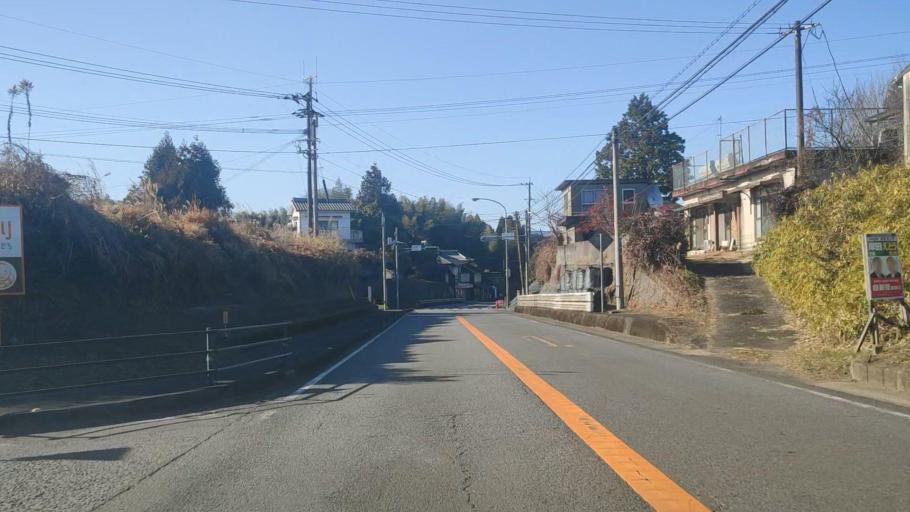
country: JP
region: Oita
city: Usuki
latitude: 33.0559
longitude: 131.6786
